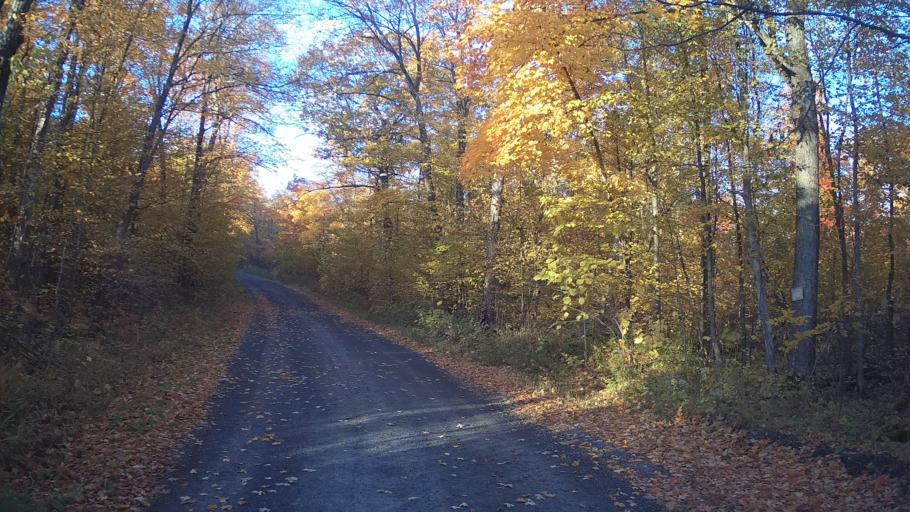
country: CA
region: Ontario
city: Arnprior
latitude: 45.3447
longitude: -76.3411
